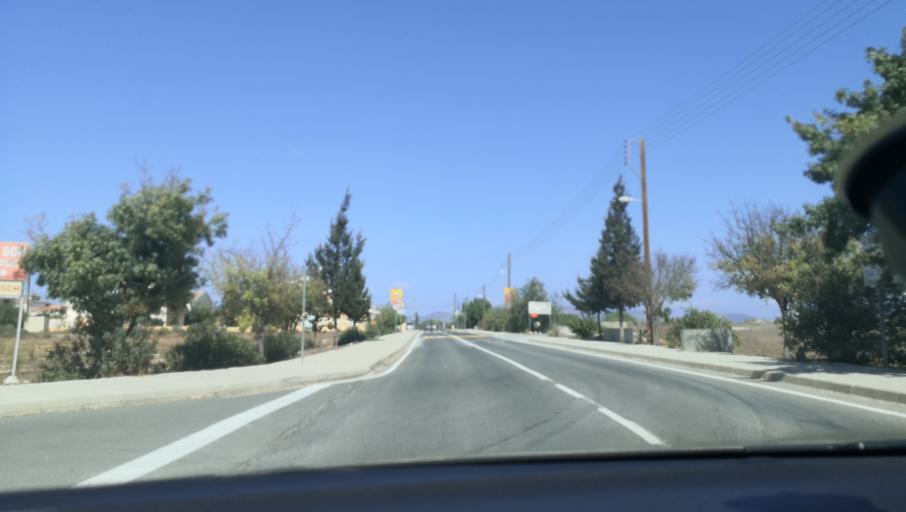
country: CY
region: Lefkosia
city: Mammari
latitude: 35.1663
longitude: 33.2027
